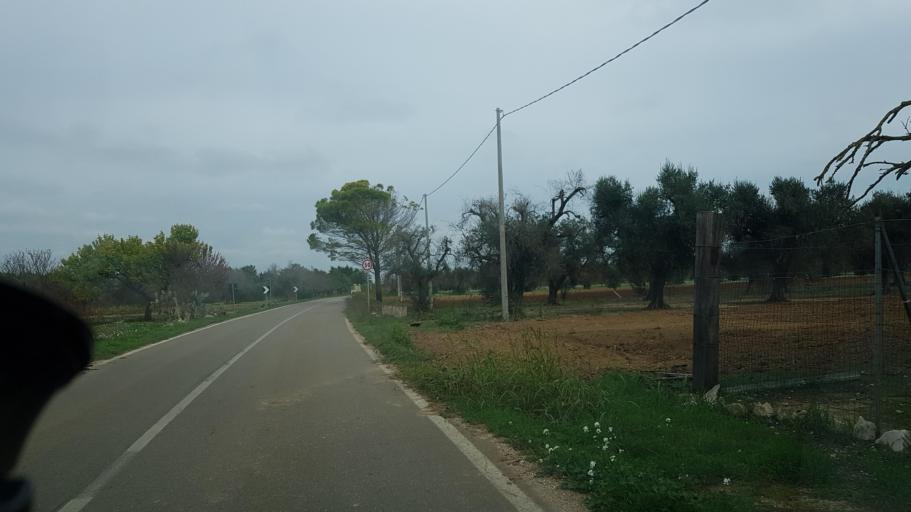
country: IT
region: Apulia
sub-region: Provincia di Lecce
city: Guagnano
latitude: 40.4162
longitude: 17.9497
